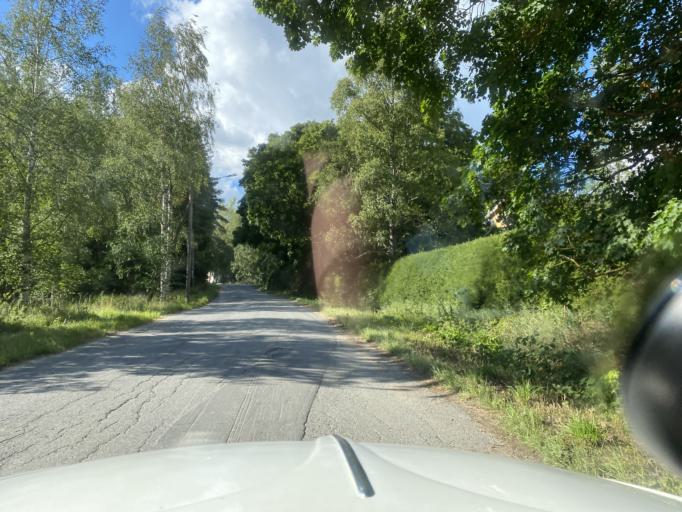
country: FI
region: Pirkanmaa
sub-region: Lounais-Pirkanmaa
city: Punkalaidun
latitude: 61.1461
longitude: 23.1969
